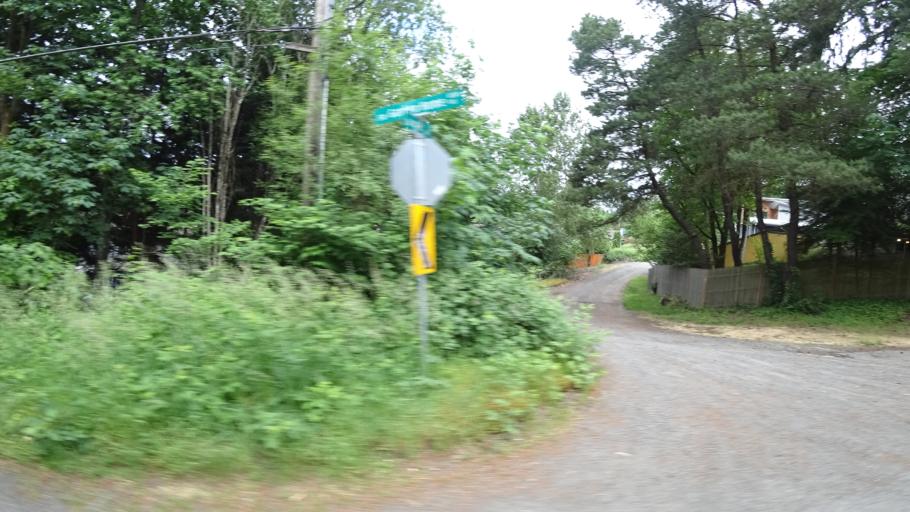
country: US
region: Oregon
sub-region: Washington County
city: Garden Home-Whitford
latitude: 45.4654
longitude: -122.7257
